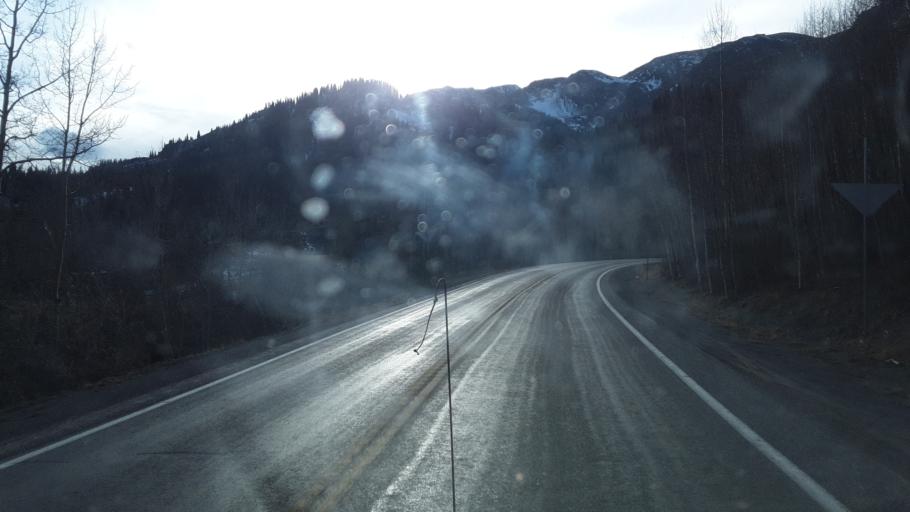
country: US
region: Colorado
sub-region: Ouray County
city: Ouray
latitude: 37.9234
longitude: -107.6984
